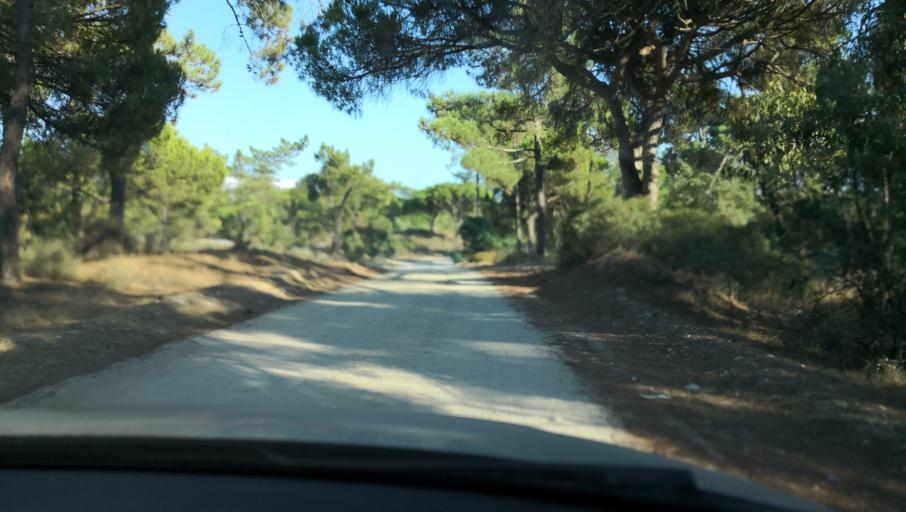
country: PT
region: Setubal
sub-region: Setubal
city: Setubal
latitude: 38.4684
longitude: -8.8743
